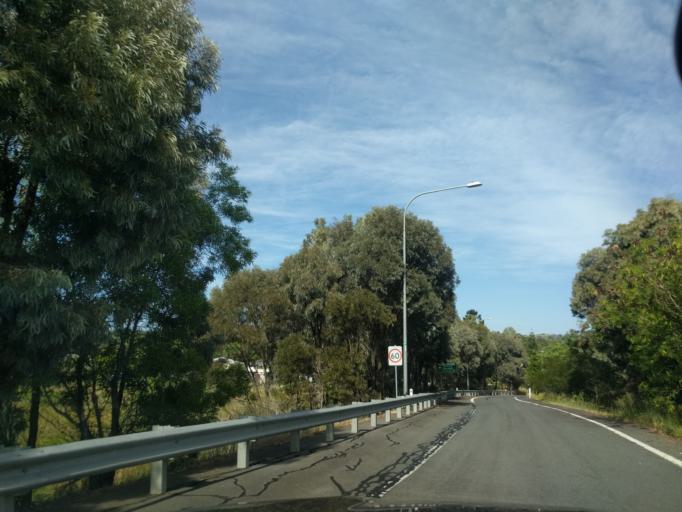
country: AU
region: Queensland
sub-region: Ipswich
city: Thagoona
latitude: -27.5638
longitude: 152.5985
